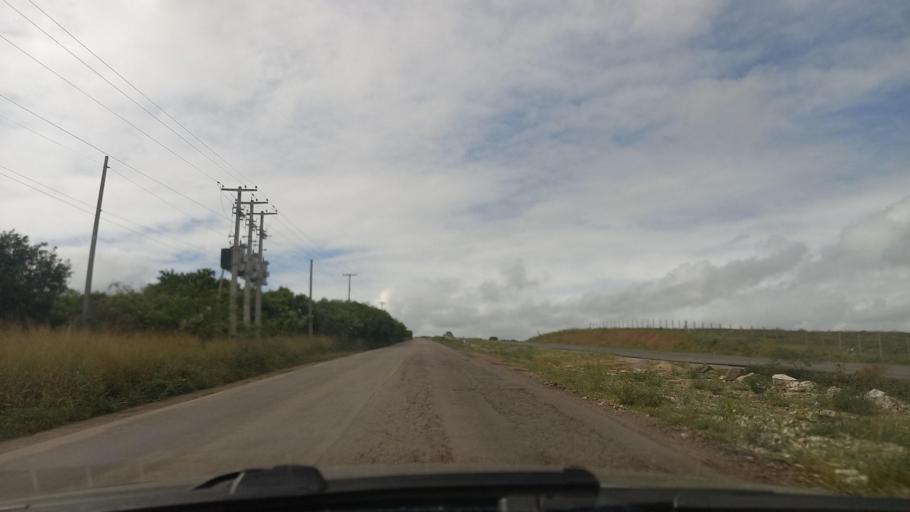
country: BR
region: Alagoas
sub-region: Batalha
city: Batalha
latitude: -9.6609
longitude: -37.1717
